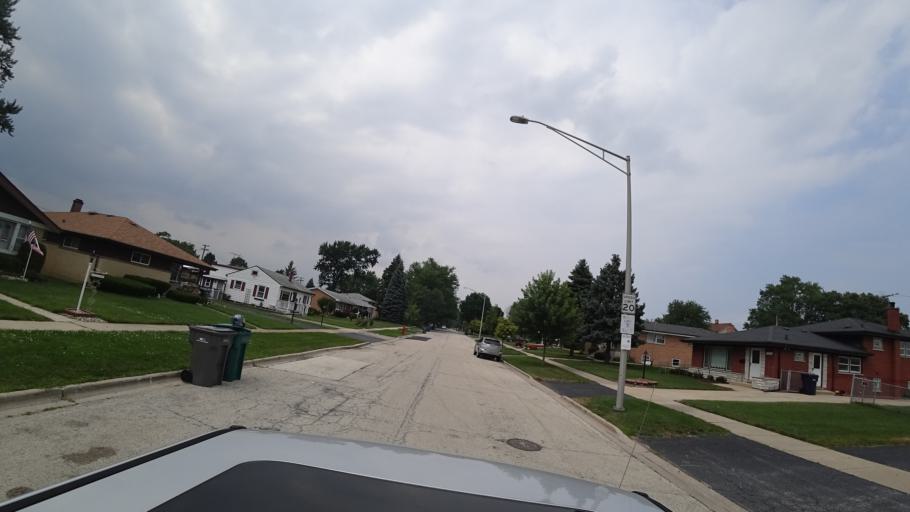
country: US
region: Illinois
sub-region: Cook County
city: Chicago Ridge
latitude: 41.6909
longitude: -87.7739
